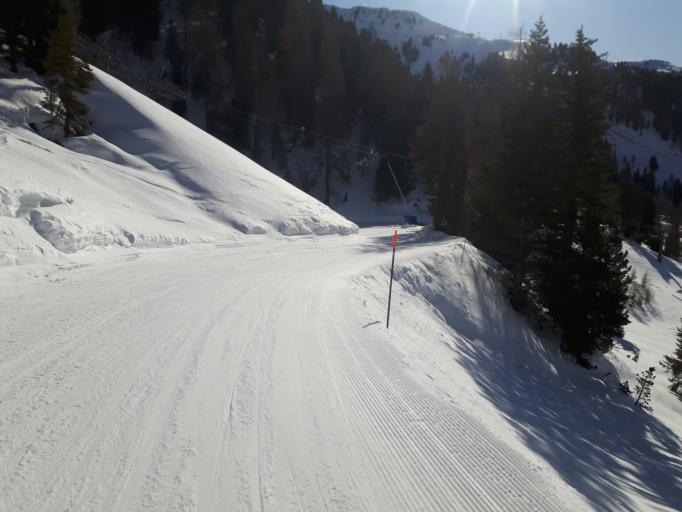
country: IT
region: Trentino-Alto Adige
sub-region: Provincia di Trento
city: Predazzo
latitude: 46.3451
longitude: 11.5537
